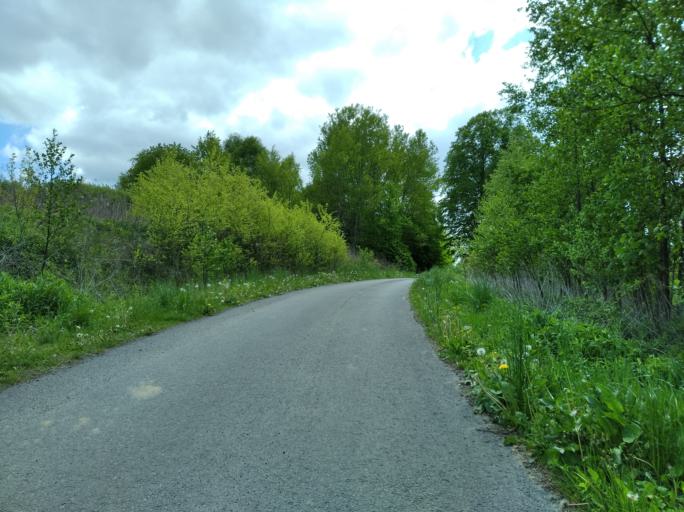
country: PL
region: Subcarpathian Voivodeship
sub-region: Powiat ropczycko-sedziszowski
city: Wielopole Skrzynskie
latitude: 49.9302
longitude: 21.6523
